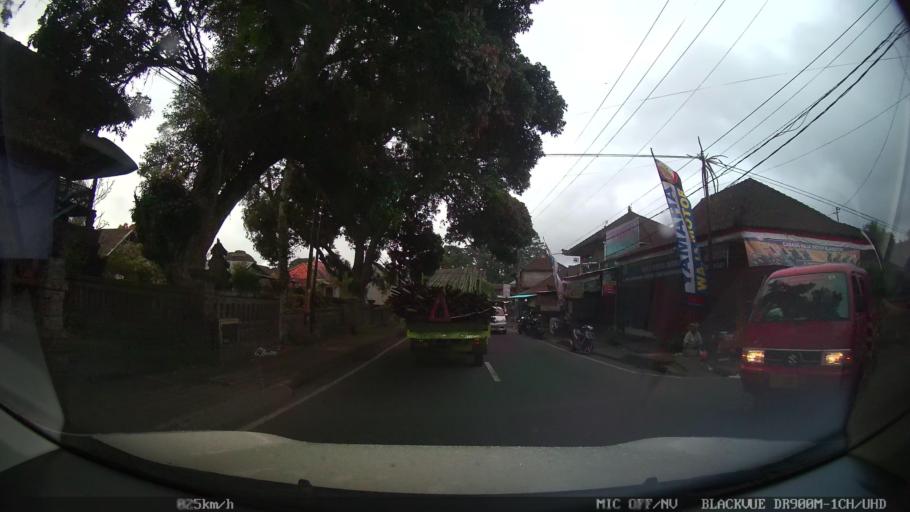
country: ID
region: Bali
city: Badung
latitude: -8.4313
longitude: 115.2455
